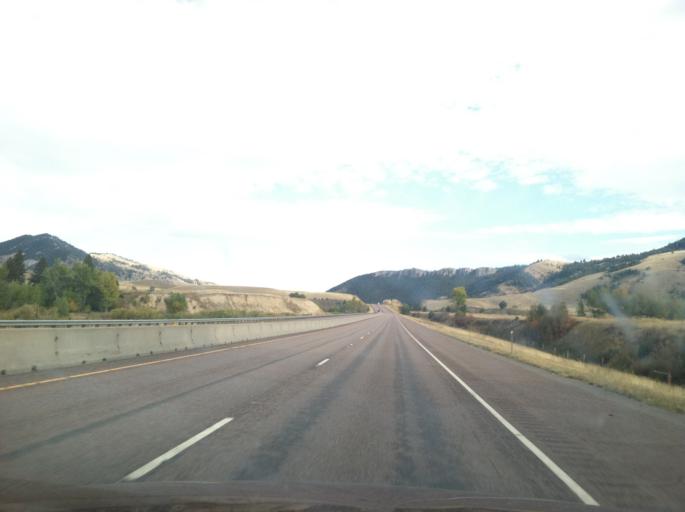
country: US
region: Montana
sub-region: Granite County
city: Philipsburg
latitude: 46.7107
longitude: -113.2646
